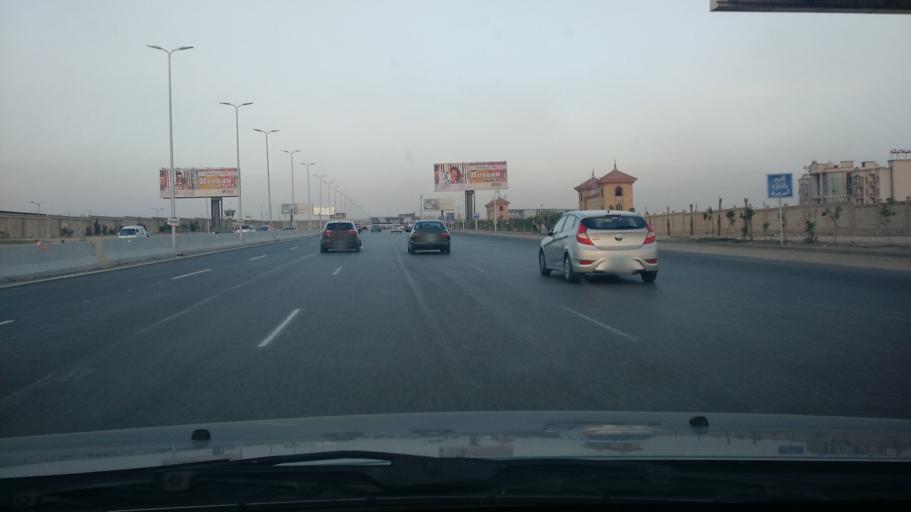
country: EG
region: Muhafazat al Qahirah
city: Cairo
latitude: 30.0244
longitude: 31.3624
